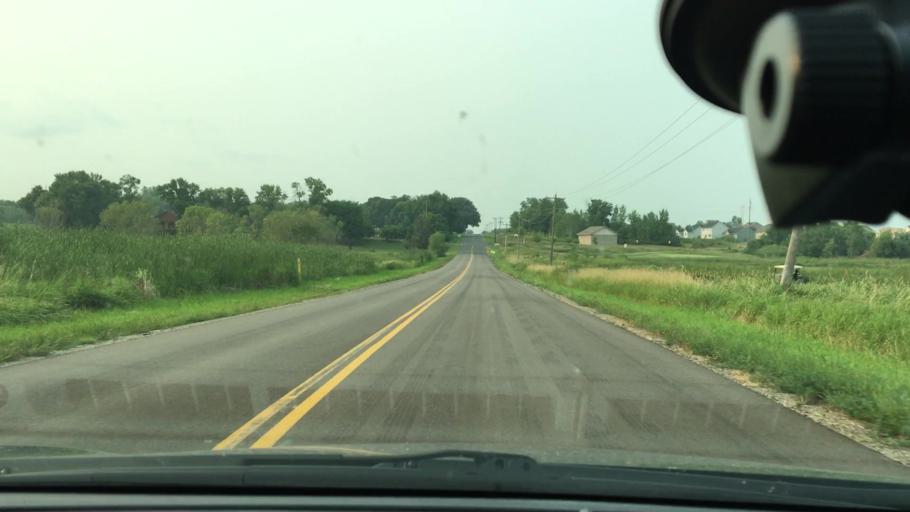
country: US
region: Minnesota
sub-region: Wright County
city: Albertville
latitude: 45.2782
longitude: -93.6841
